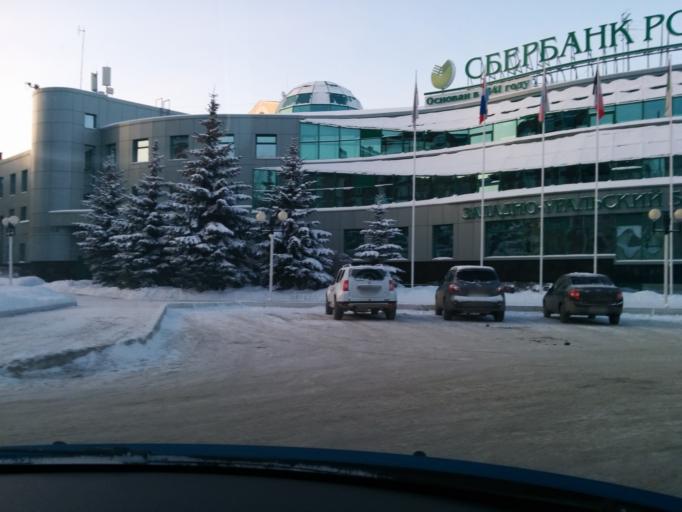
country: RU
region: Perm
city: Perm
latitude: 58.0176
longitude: 56.2414
